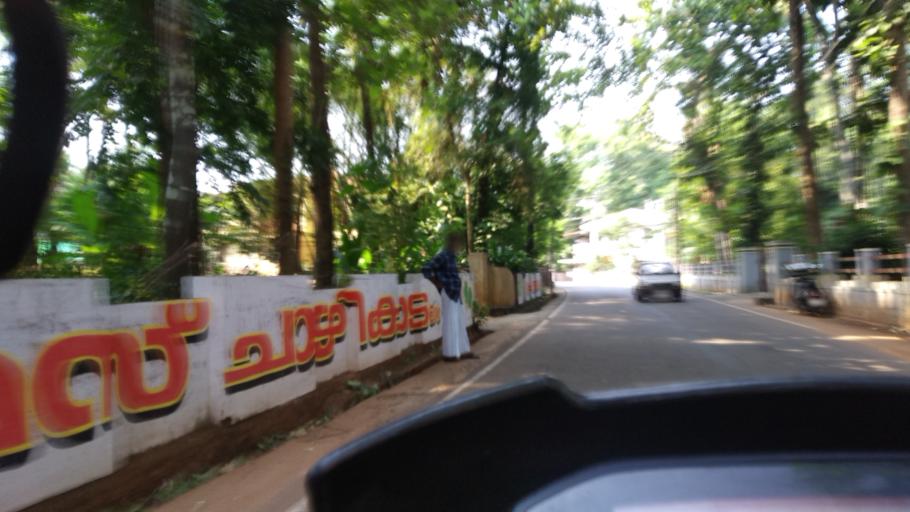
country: IN
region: Kerala
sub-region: Ernakulam
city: Piravam
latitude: 9.8722
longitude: 76.4973
